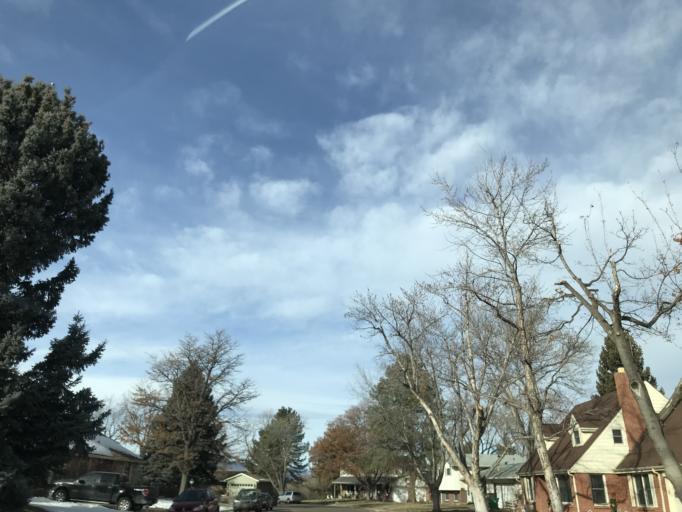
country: US
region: Colorado
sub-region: Arapahoe County
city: Columbine Valley
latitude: 39.5939
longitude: -105.0188
